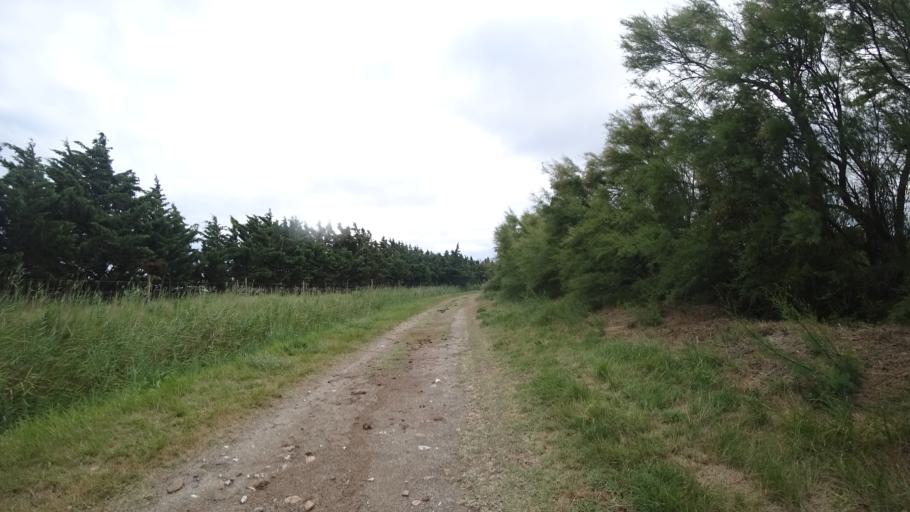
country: FR
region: Languedoc-Roussillon
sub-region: Departement des Pyrenees-Orientales
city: Le Barcares
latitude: 42.7788
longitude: 3.0173
